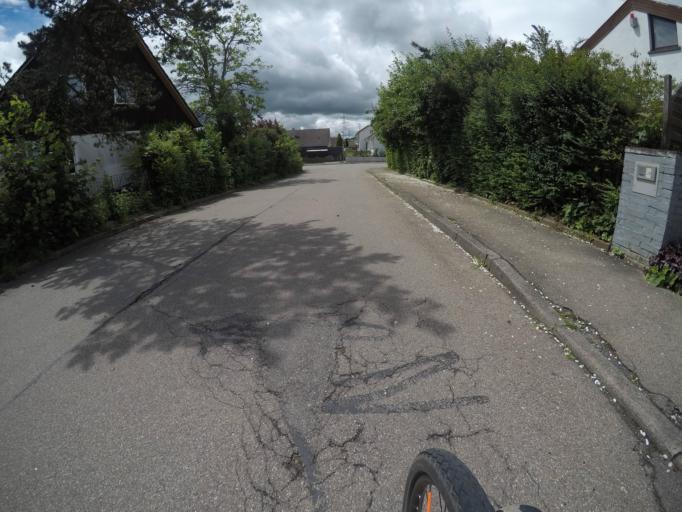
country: DE
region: Baden-Wuerttemberg
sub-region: Regierungsbezirk Stuttgart
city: Deckenpfronn
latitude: 48.6207
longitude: 8.8309
